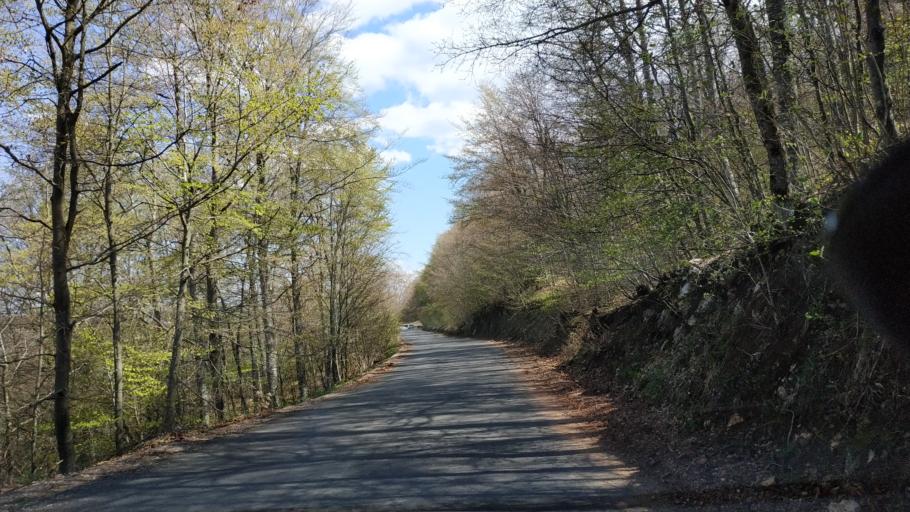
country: RS
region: Central Serbia
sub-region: Zajecarski Okrug
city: Soko Banja
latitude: 43.5848
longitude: 21.8891
